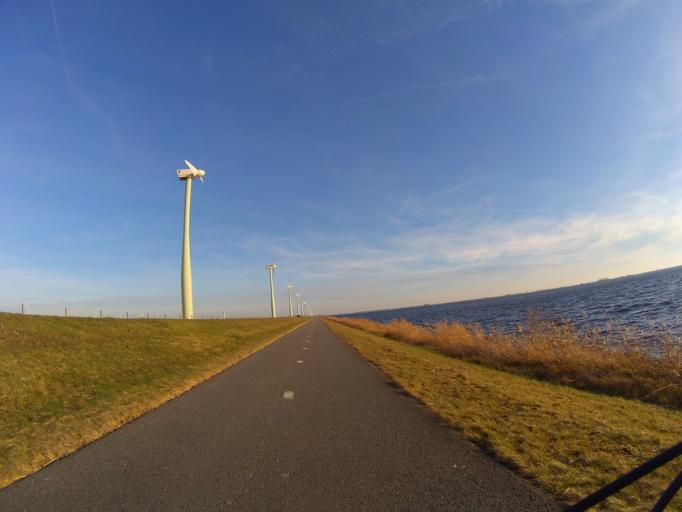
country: NL
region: Utrecht
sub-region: Gemeente Bunschoten
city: Spakenburg
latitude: 52.2890
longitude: 5.3432
